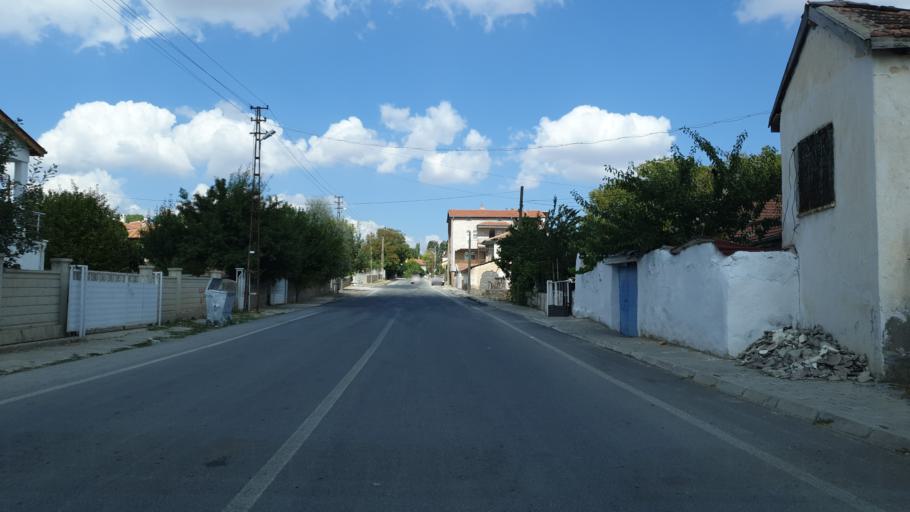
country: TR
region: Kayseri
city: Felahiye
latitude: 39.1110
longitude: 35.6072
